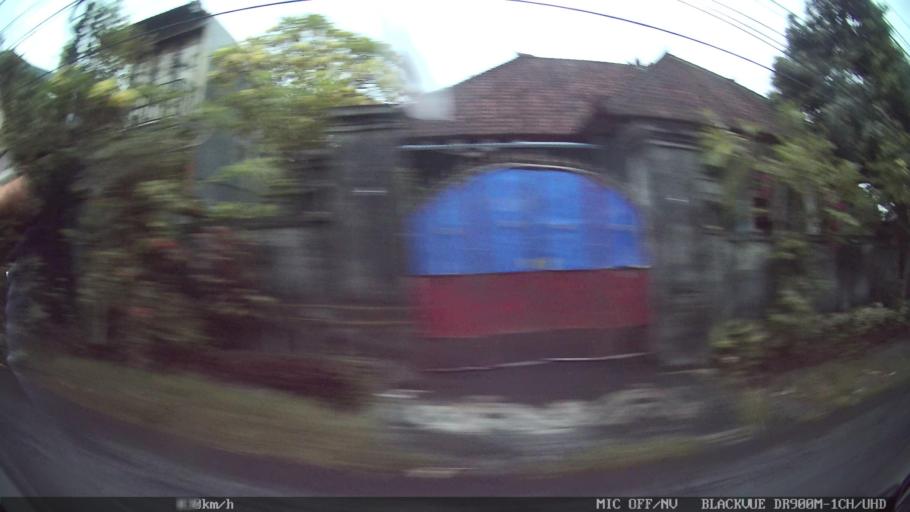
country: ID
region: Bali
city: Banjar Kertajiwa
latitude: -8.6183
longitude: 115.2663
